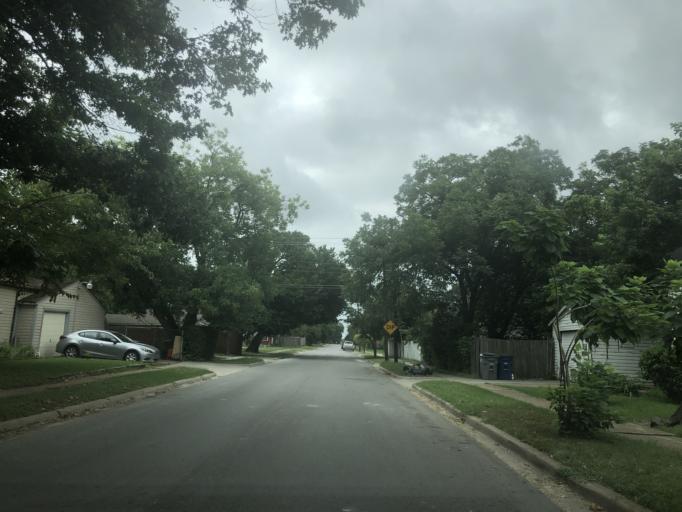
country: US
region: Texas
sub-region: Dallas County
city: University Park
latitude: 32.8682
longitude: -96.8530
